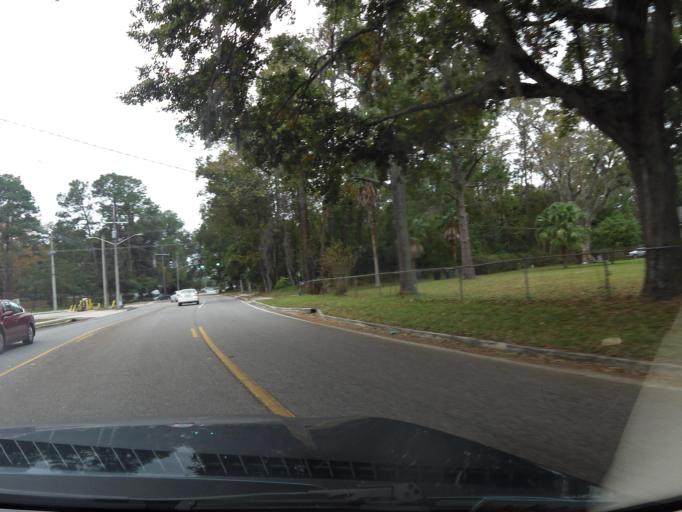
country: US
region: Florida
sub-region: Duval County
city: Jacksonville
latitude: 30.2854
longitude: -81.6107
